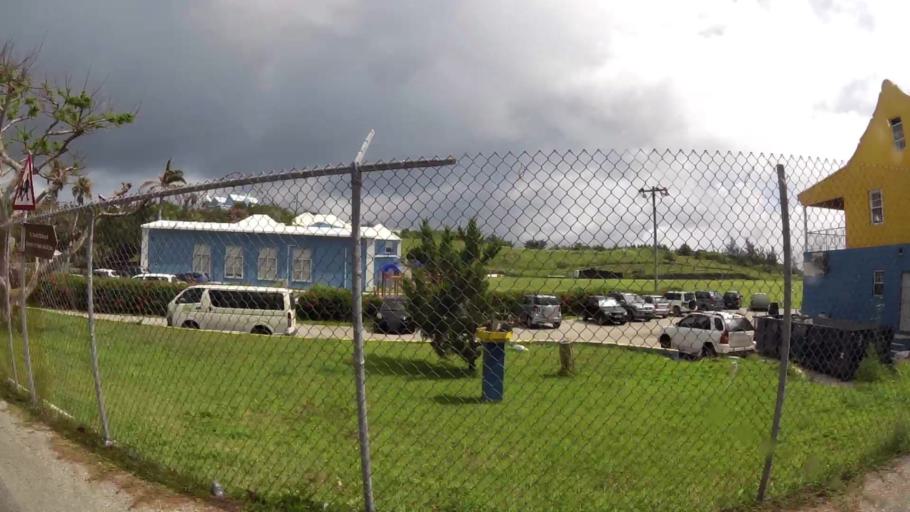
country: BM
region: Saint George
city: Saint George
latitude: 32.3694
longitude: -64.6519
